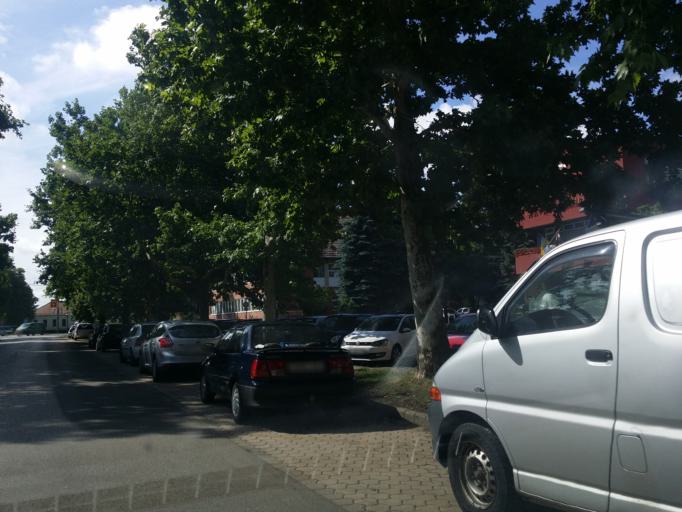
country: HU
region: Heves
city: Heves
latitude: 47.5972
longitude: 20.2871
